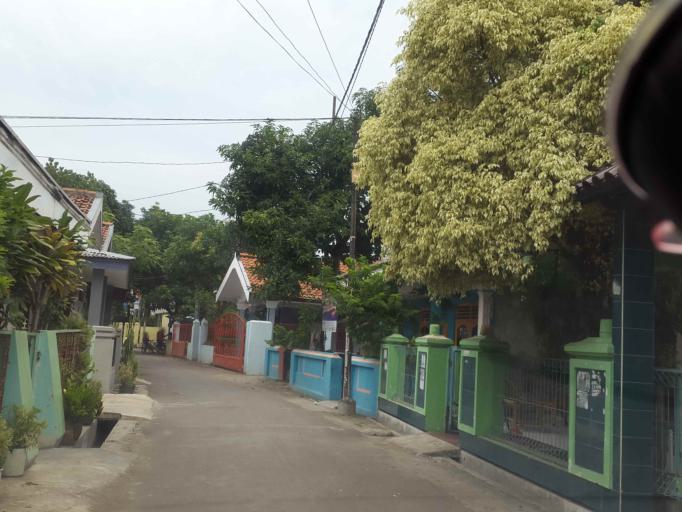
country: ID
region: Central Java
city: Dukuhturi
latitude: -6.8790
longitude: 109.0954
